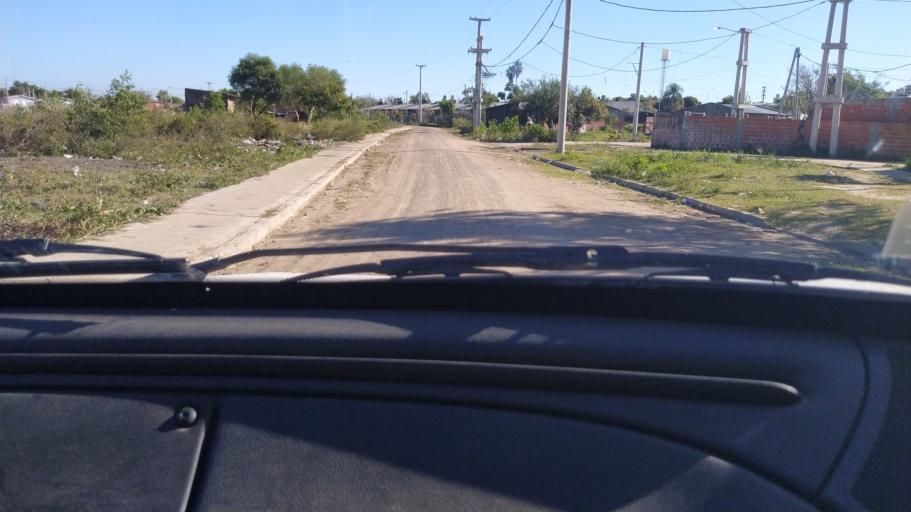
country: AR
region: Corrientes
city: Corrientes
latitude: -27.4973
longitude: -58.8016
